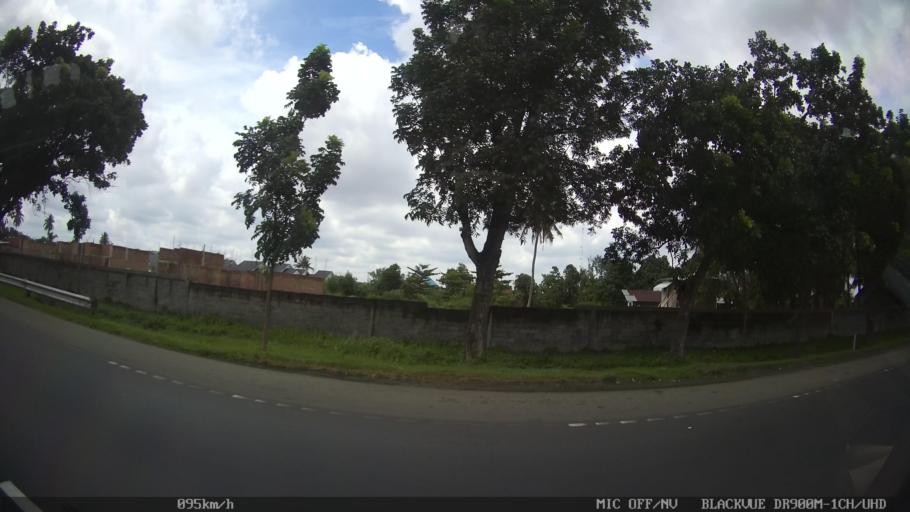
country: ID
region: North Sumatra
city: Medan
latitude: 3.6201
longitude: 98.7202
